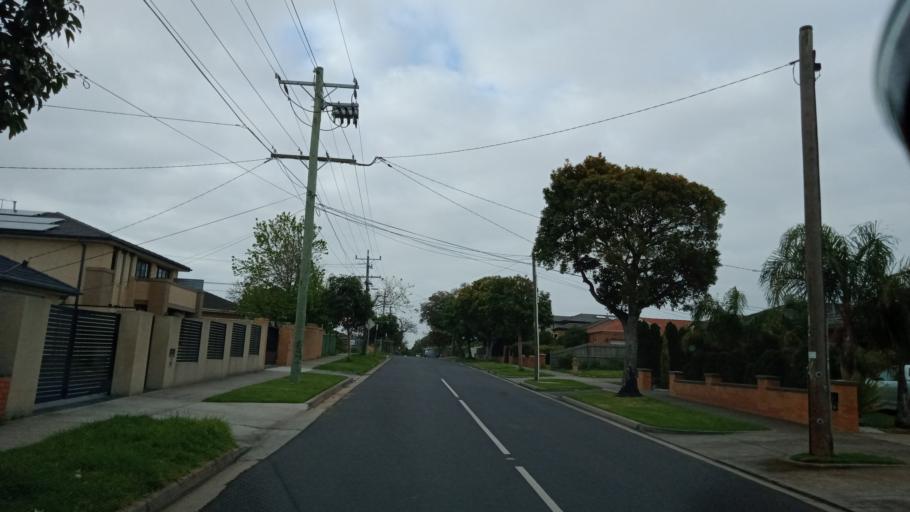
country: AU
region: Victoria
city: McKinnon
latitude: -37.9275
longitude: 145.0668
